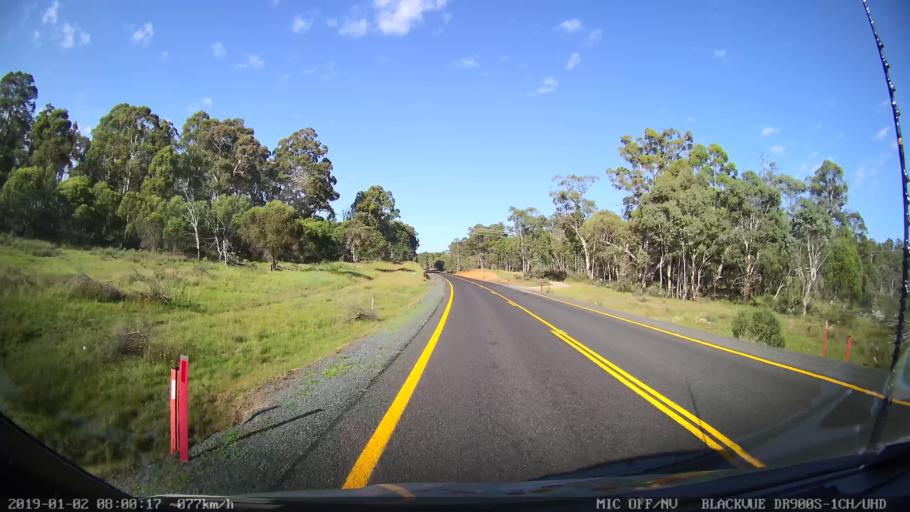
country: AU
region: New South Wales
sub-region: Tumut Shire
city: Tumut
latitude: -35.6440
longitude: 148.4473
